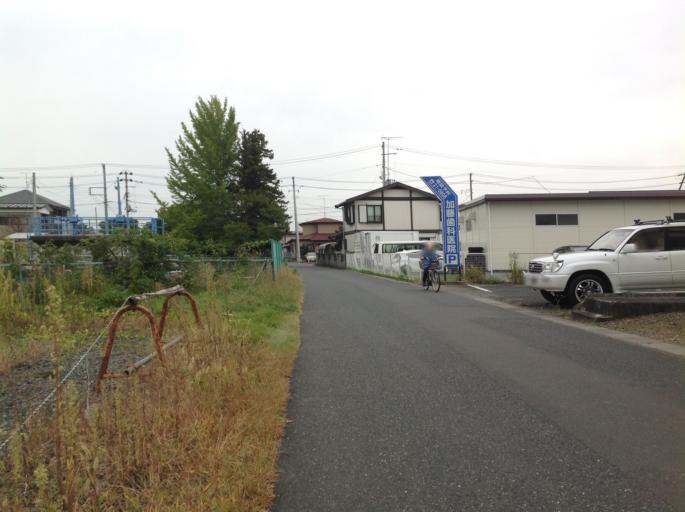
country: JP
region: Iwate
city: Ichinoseki
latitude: 38.9352
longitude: 141.1204
